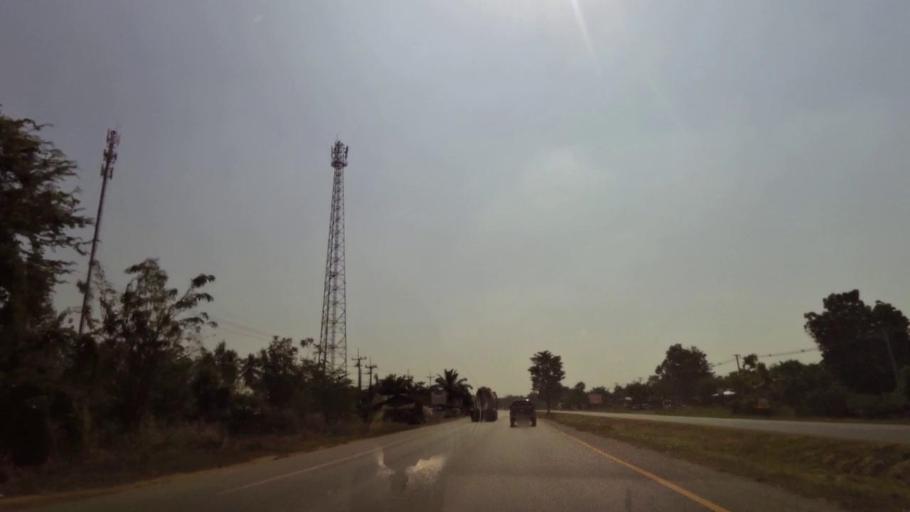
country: TH
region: Phichit
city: Bueng Na Rang
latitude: 16.3458
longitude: 100.1286
